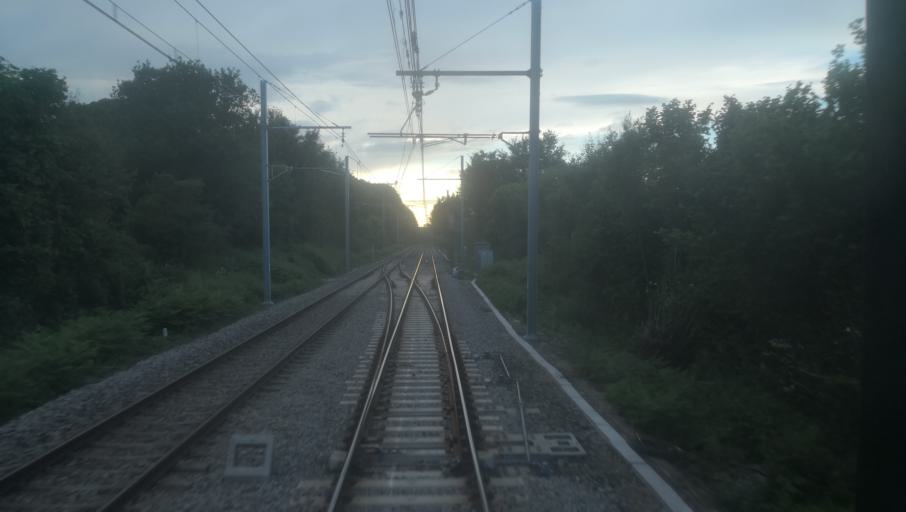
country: FR
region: Limousin
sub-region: Departement de la Creuse
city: La Souterraine
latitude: 46.2491
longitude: 1.4830
